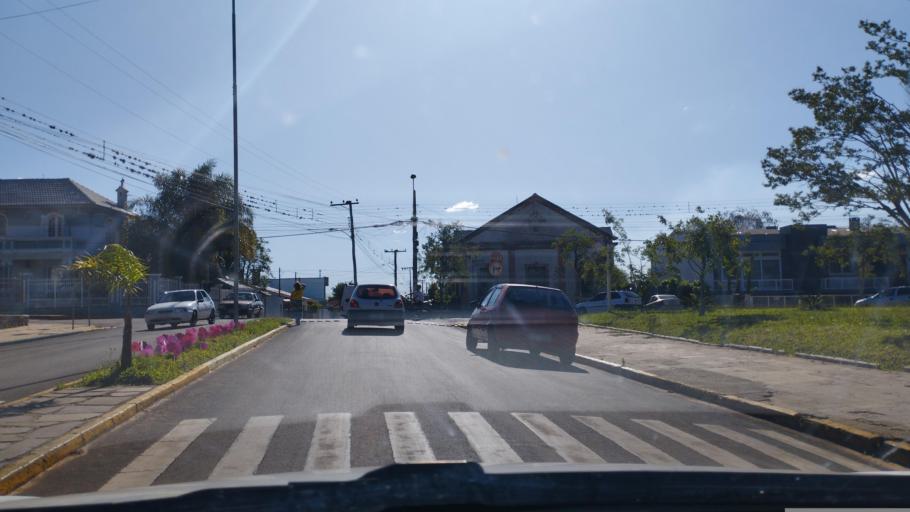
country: BR
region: Rio Grande do Sul
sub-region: Tupancireta
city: Tupancireta
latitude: -29.0856
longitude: -53.8359
